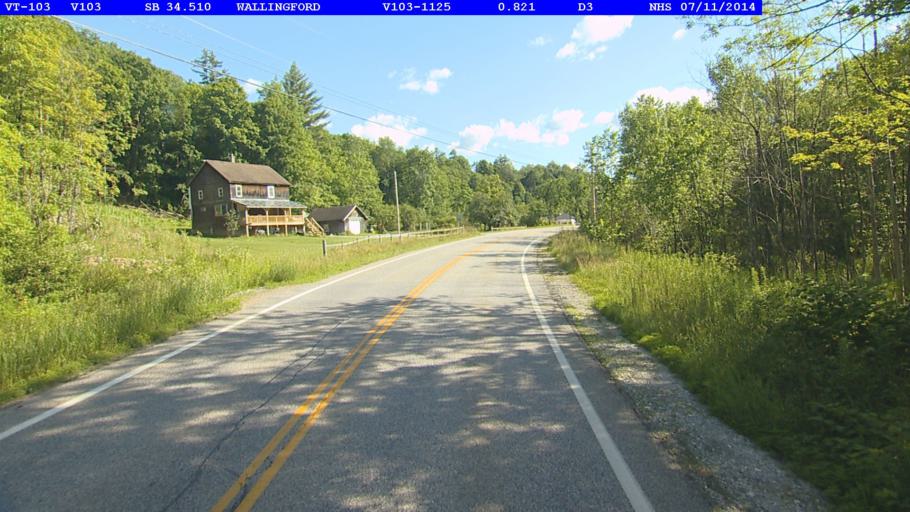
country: US
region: Vermont
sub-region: Rutland County
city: Rutland
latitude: 43.4619
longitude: -72.8732
